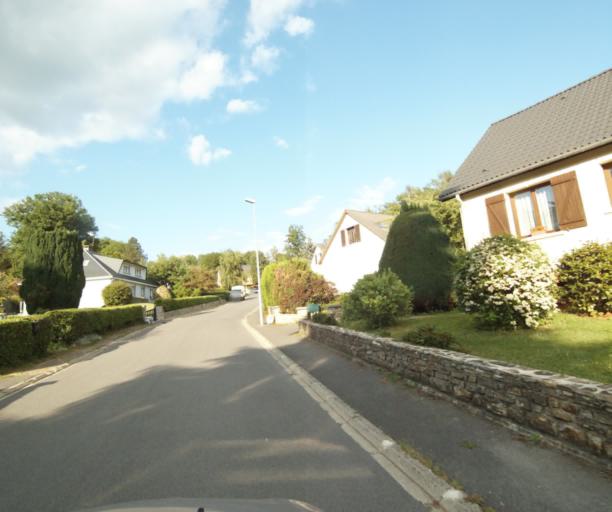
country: FR
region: Champagne-Ardenne
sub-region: Departement des Ardennes
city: Charleville-Mezieres
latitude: 49.7956
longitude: 4.7081
